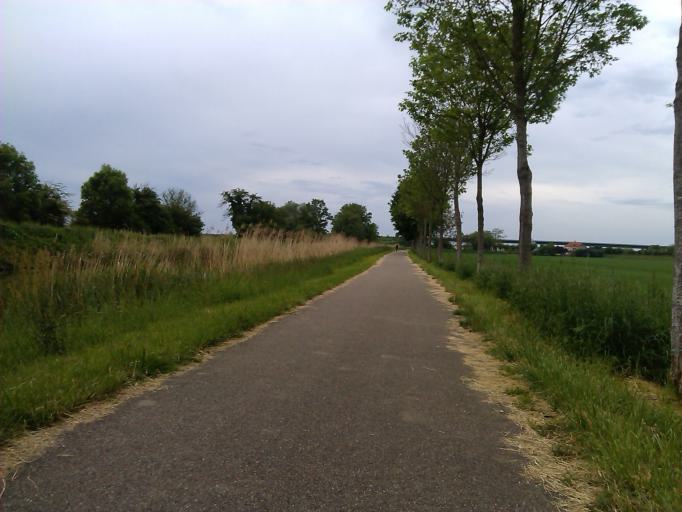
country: FR
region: Franche-Comte
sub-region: Departement du Jura
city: Choisey
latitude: 47.0571
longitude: 5.4494
